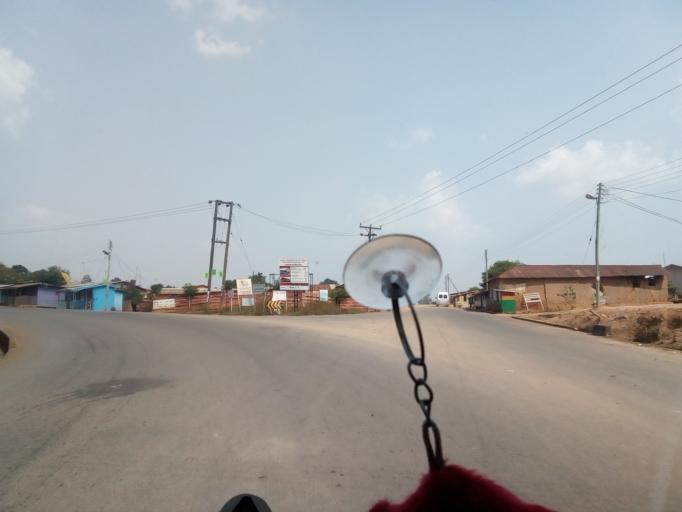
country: GH
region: Eastern
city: Suhum
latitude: 6.0449
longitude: -0.4133
